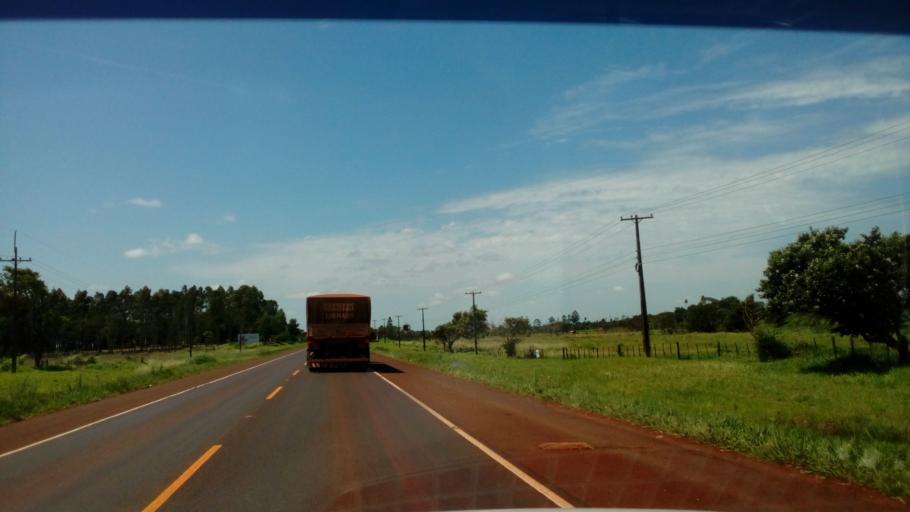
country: PY
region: Alto Parana
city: Colonia Yguazu
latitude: -25.5126
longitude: -54.8995
